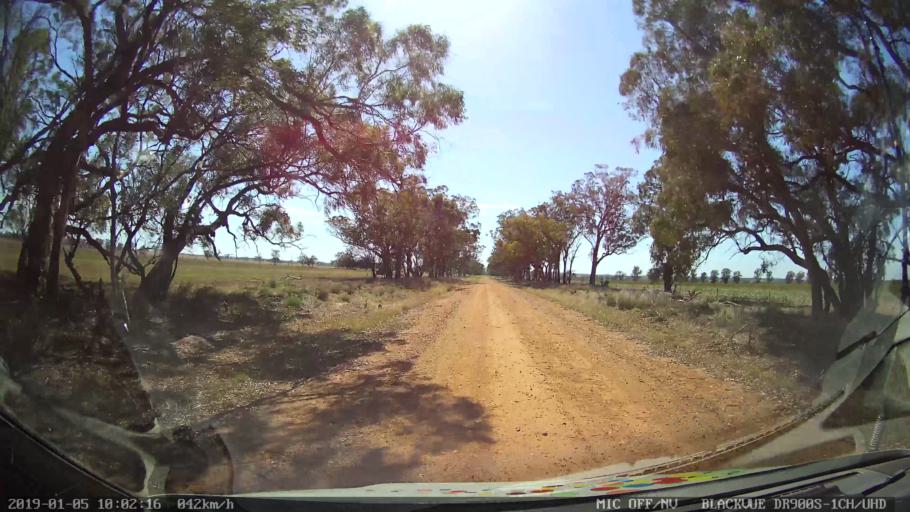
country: AU
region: New South Wales
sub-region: Gilgandra
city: Gilgandra
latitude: -31.6706
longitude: 148.8421
